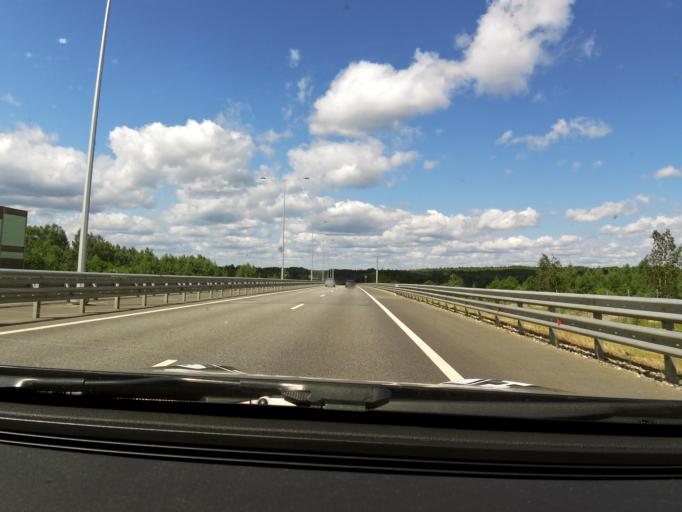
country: RU
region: Tverskaya
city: Vydropuzhsk
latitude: 57.3680
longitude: 34.6548
